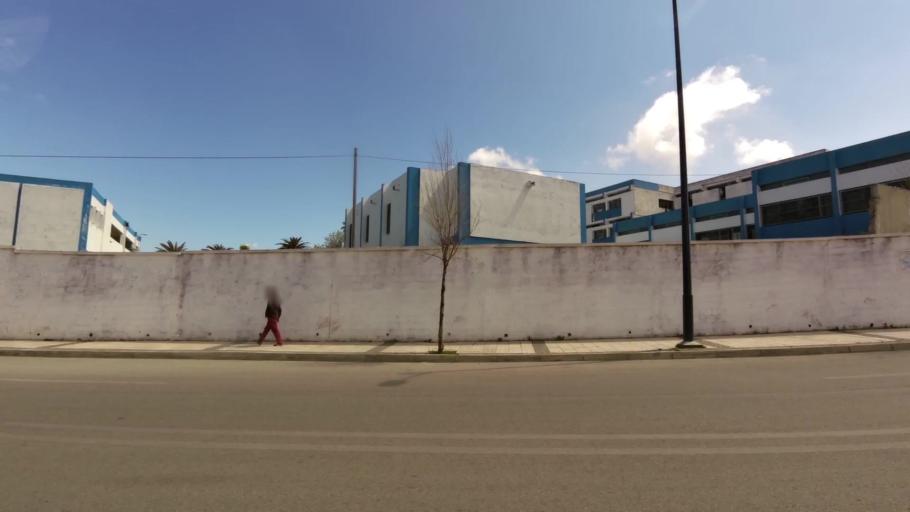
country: MA
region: Tanger-Tetouan
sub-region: Tanger-Assilah
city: Tangier
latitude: 35.7737
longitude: -5.8411
